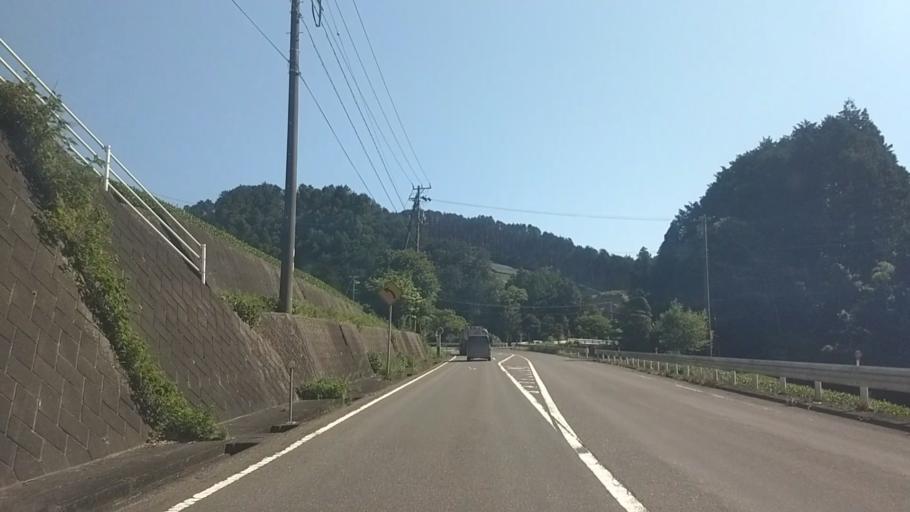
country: JP
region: Shizuoka
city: Fujinomiya
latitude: 35.1704
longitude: 138.5234
